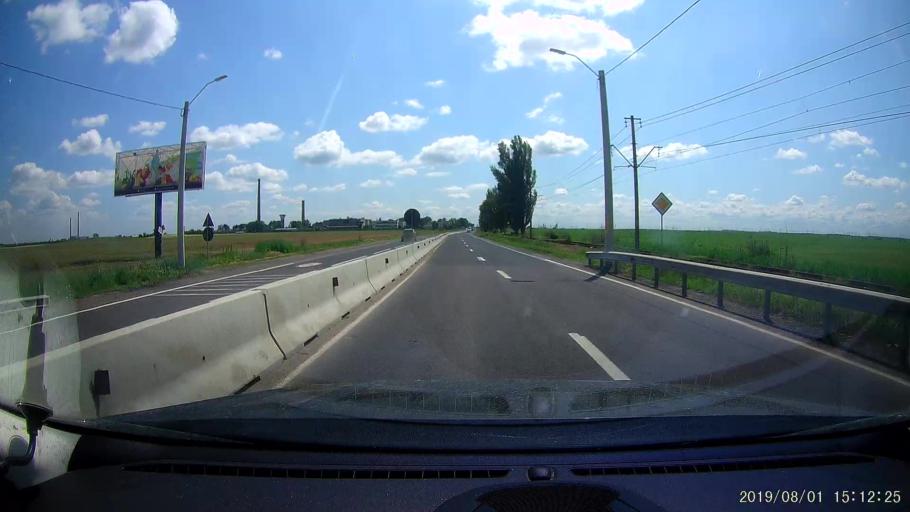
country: RO
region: Braila
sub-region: Comuna Chiscani
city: Lacu Sarat
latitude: 45.2066
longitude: 27.9139
